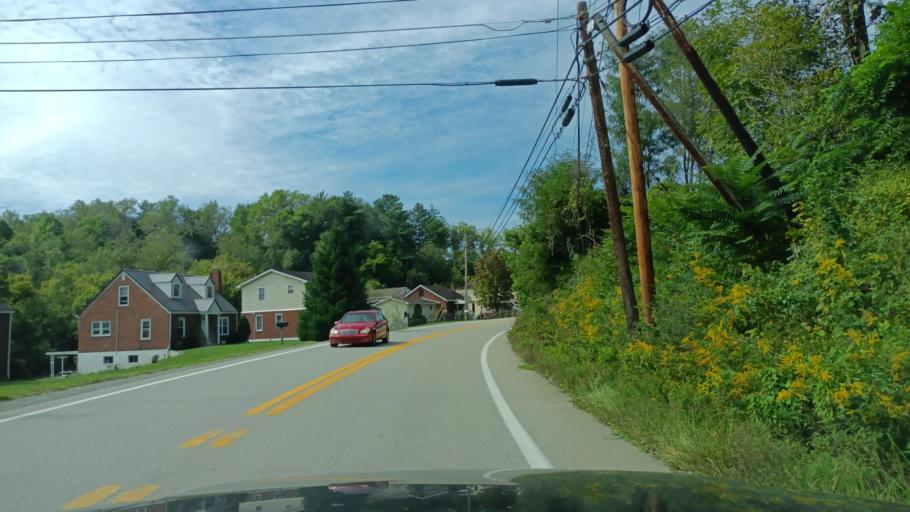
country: US
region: West Virginia
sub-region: Harrison County
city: Bridgeport
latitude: 39.2956
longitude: -80.2070
